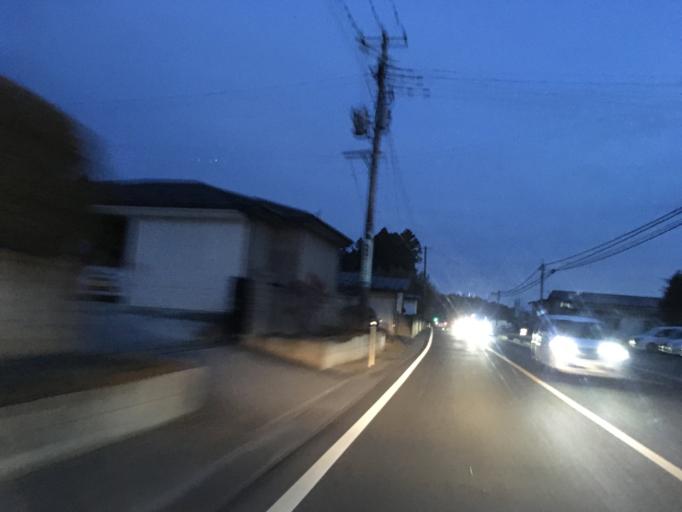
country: JP
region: Miyagi
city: Wakuya
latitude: 38.6932
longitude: 141.1677
